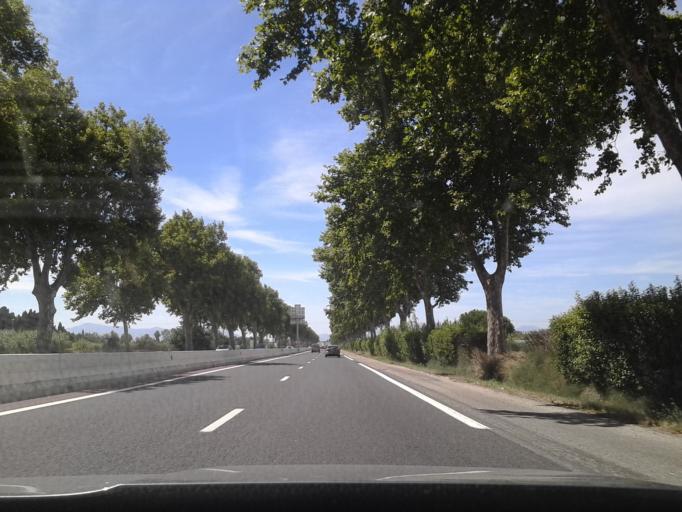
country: FR
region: Languedoc-Roussillon
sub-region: Departement des Pyrenees-Orientales
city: Rivesaltes
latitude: 42.7663
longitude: 2.8993
